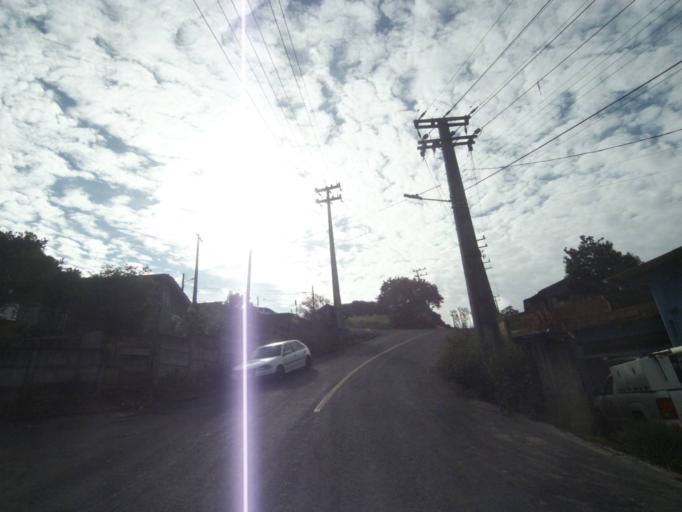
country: BR
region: Parana
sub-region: Telemaco Borba
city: Telemaco Borba
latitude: -24.3394
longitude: -50.6146
